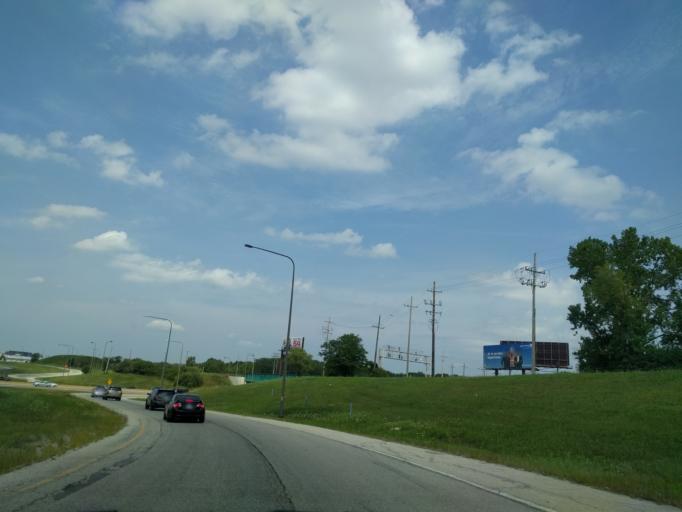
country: US
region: Illinois
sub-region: Cook County
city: Rosemont
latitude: 41.9801
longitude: -87.8766
